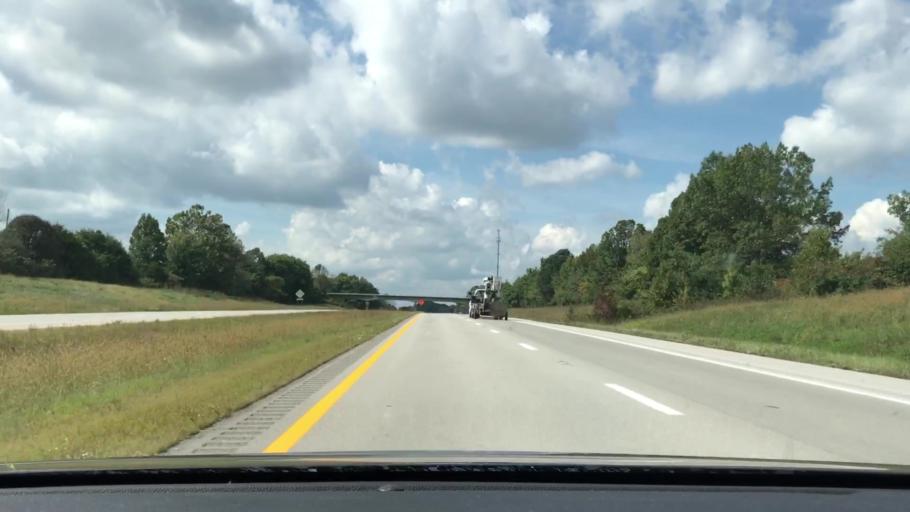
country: US
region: Kentucky
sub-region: Russell County
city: Russell Springs
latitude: 37.0872
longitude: -84.9021
